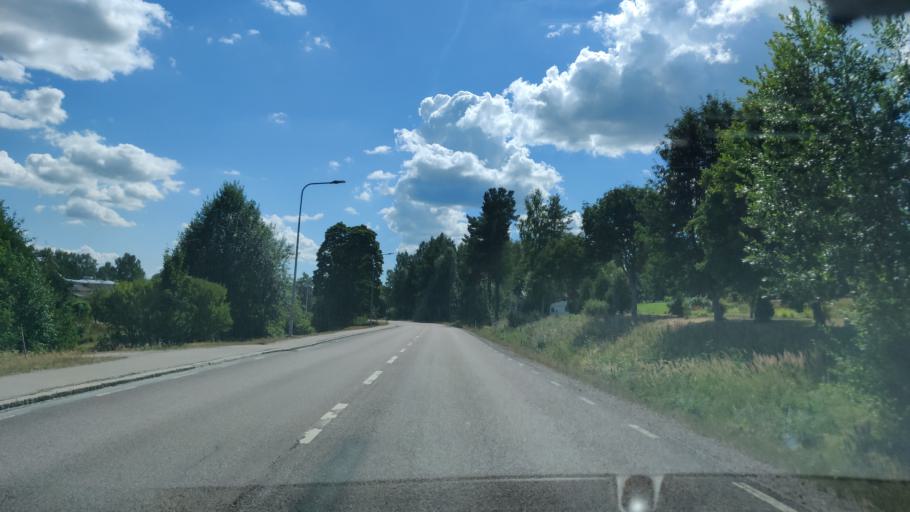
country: SE
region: Vaermland
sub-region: Hagfors Kommun
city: Ekshaerad
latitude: 60.1831
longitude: 13.4961
